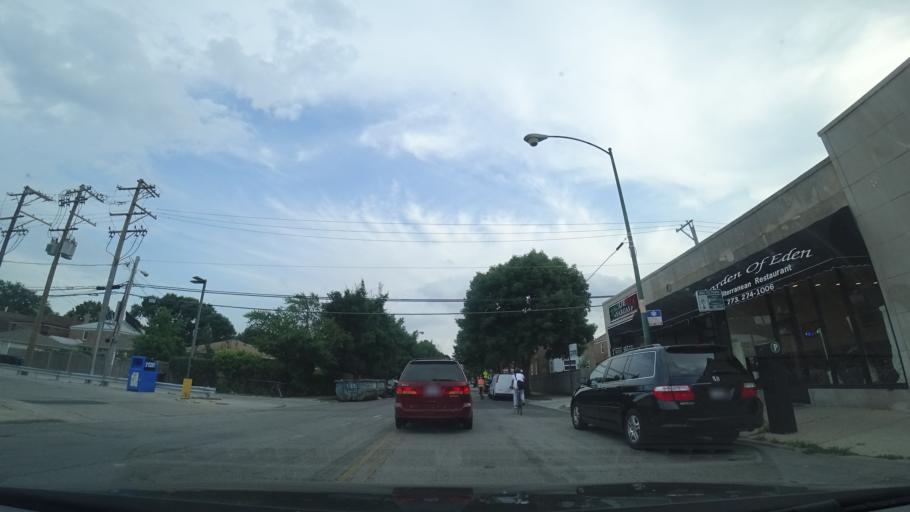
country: US
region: Illinois
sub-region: Cook County
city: Evanston
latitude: 42.0118
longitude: -87.6998
